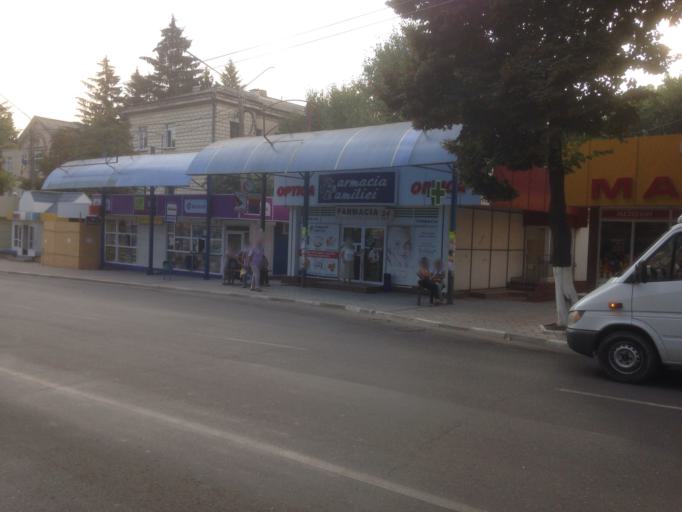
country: MD
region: Balti
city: Balti
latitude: 47.7639
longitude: 27.9306
